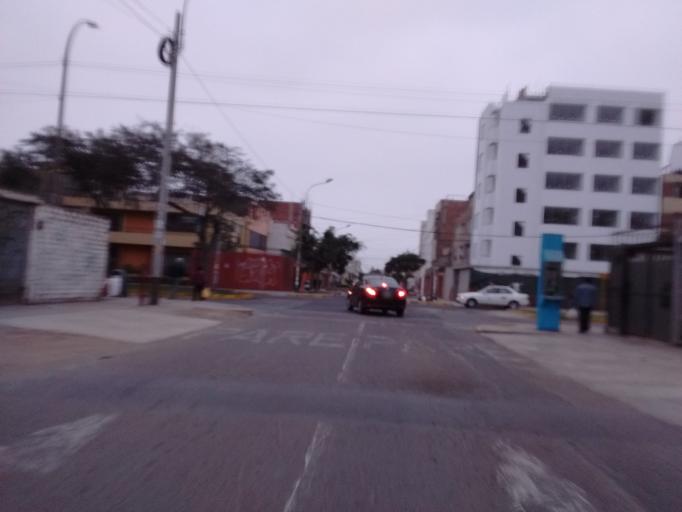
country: PE
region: Callao
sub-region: Callao
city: Callao
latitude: -12.0527
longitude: -77.0740
